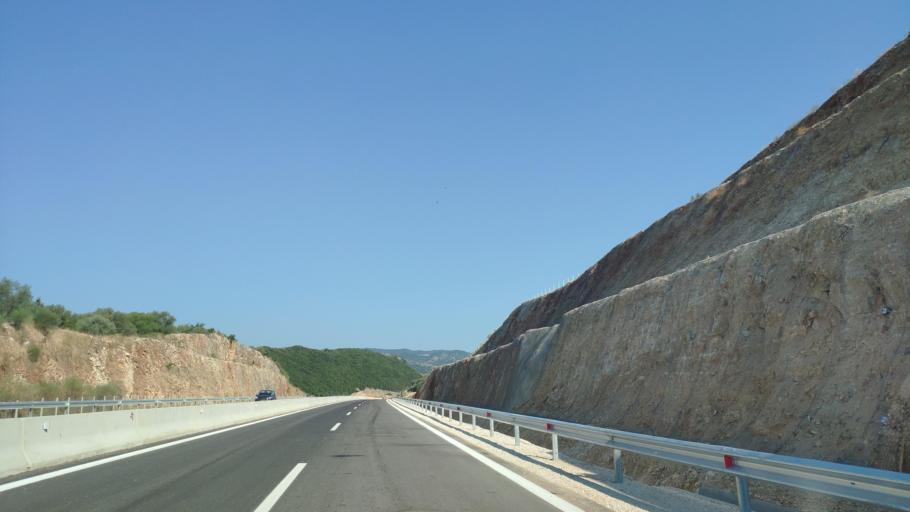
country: GR
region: West Greece
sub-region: Nomos Aitolias kai Akarnanias
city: Stanos
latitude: 38.7777
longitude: 21.1524
